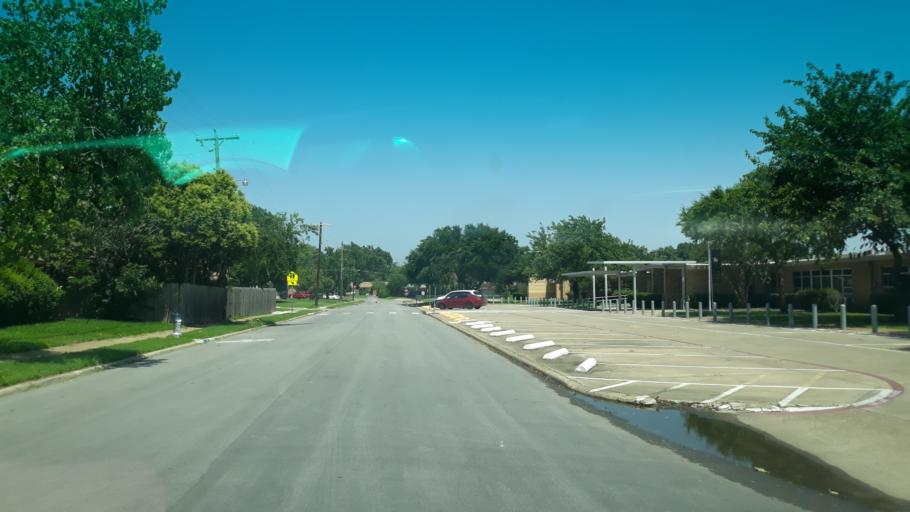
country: US
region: Texas
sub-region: Dallas County
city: Irving
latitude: 32.8540
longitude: -96.9668
